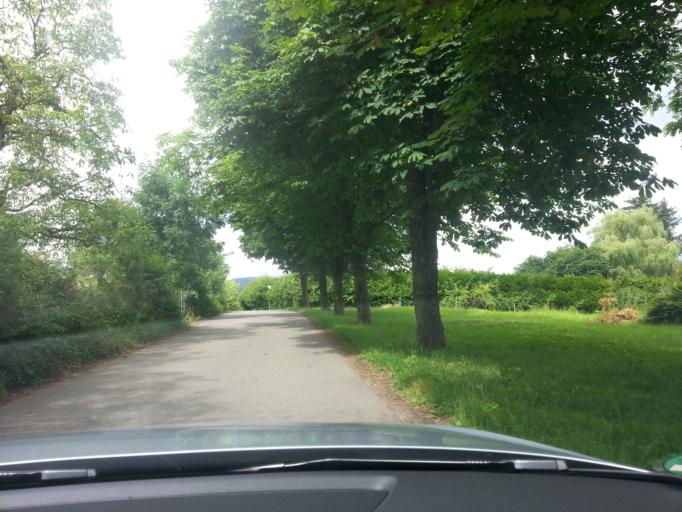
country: LU
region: Grevenmacher
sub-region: Canton de Remich
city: Bous
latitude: 49.5384
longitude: 6.3386
